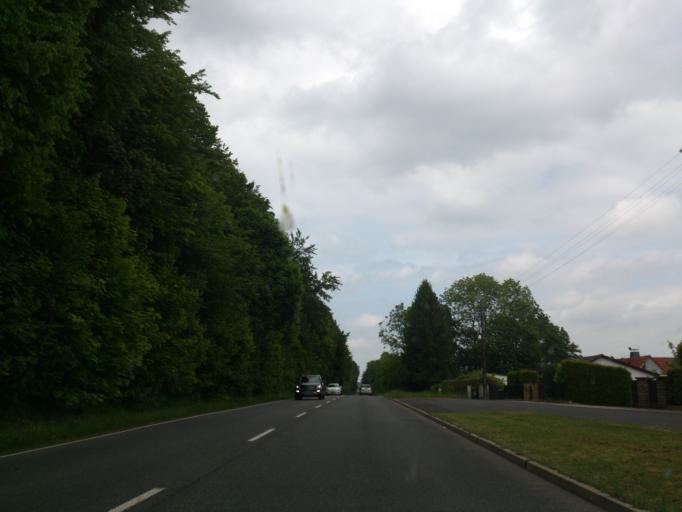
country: DE
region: Hesse
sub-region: Regierungsbezirk Kassel
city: Vellmar
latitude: 51.3416
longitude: 9.4156
